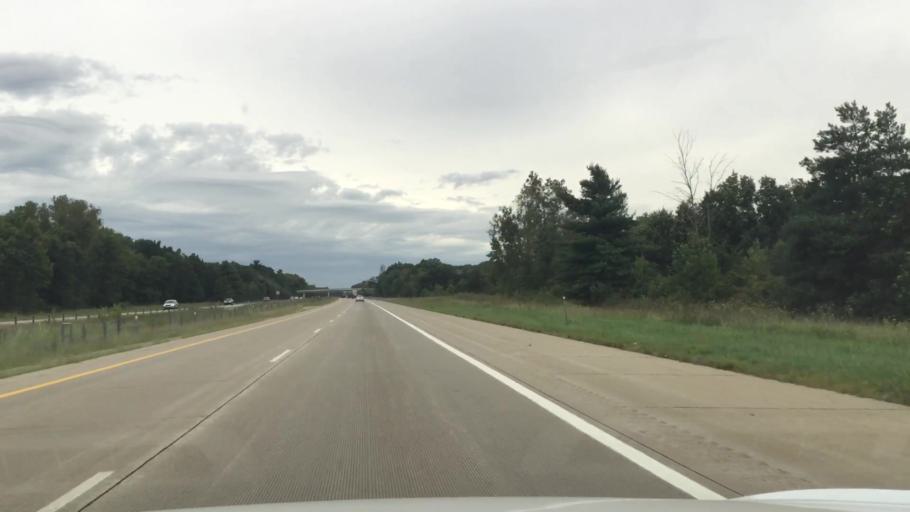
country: US
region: Michigan
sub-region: Saint Clair County
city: Saint Clair
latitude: 42.8405
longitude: -82.5889
